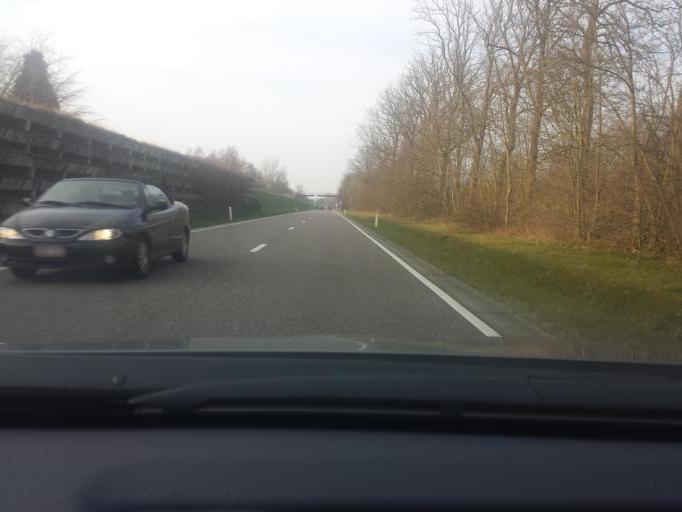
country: BE
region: Flanders
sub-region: Provincie Limburg
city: Maasmechelen
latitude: 50.9698
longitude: 5.7073
